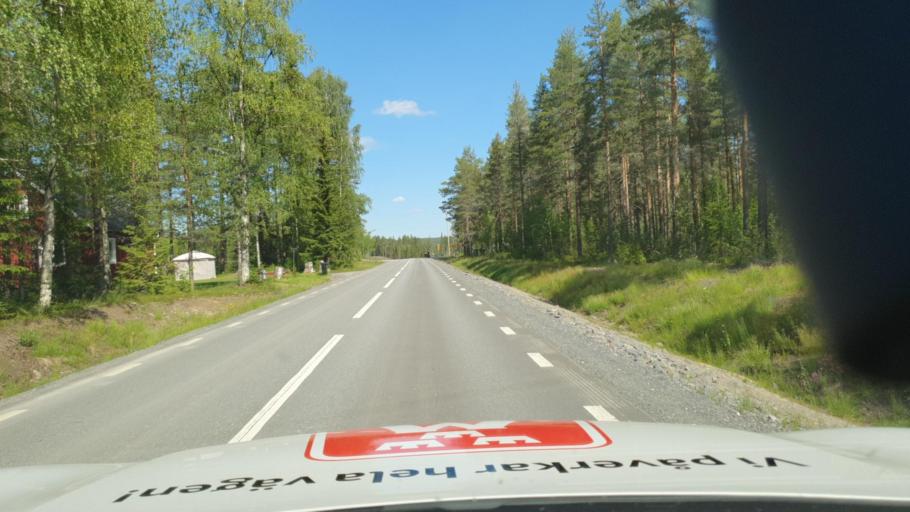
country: SE
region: Vaesterbotten
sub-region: Skelleftea Kommun
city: Boliden
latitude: 64.7815
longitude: 20.3395
